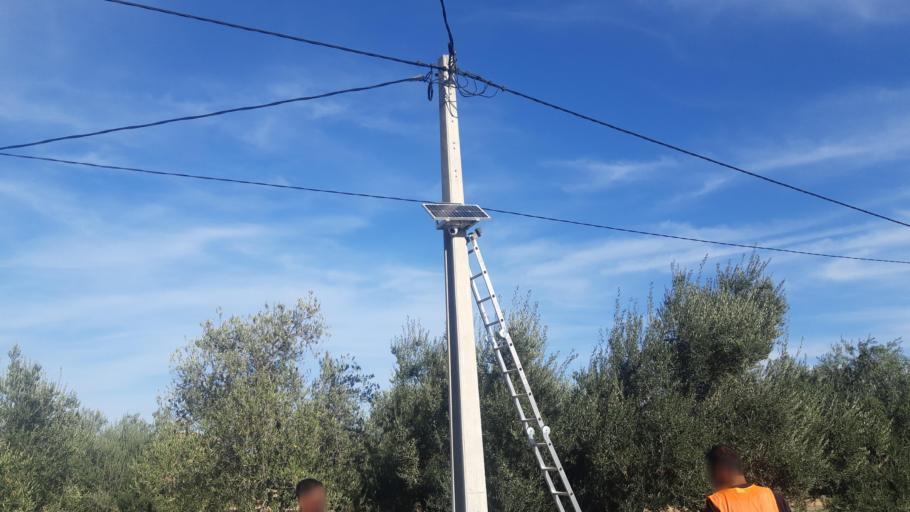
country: TN
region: Al Mahdiyah
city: El Jem
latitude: 35.2968
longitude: 10.6918
